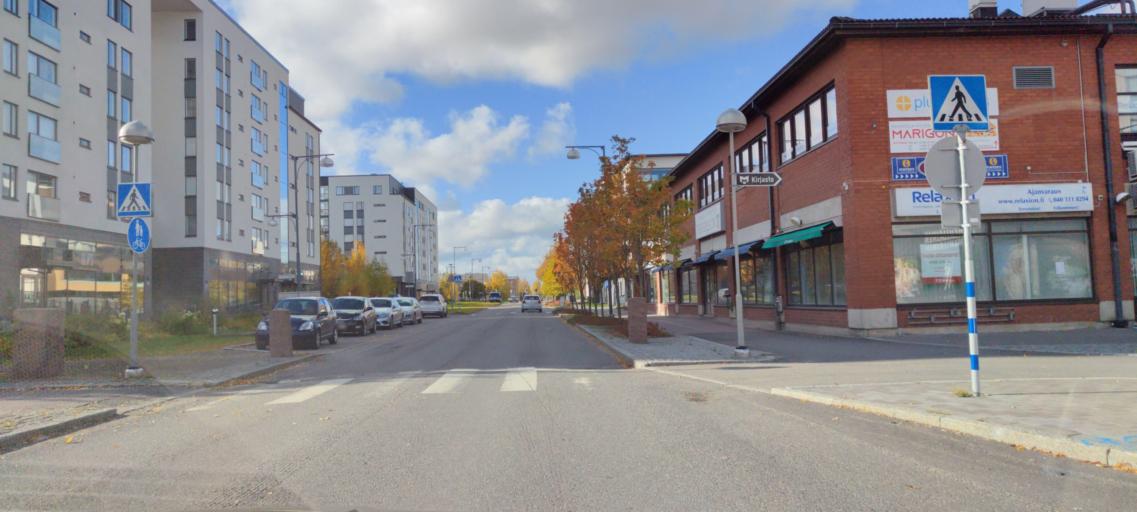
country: FI
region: Varsinais-Suomi
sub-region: Turku
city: Kaarina
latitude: 60.4072
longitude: 22.3675
